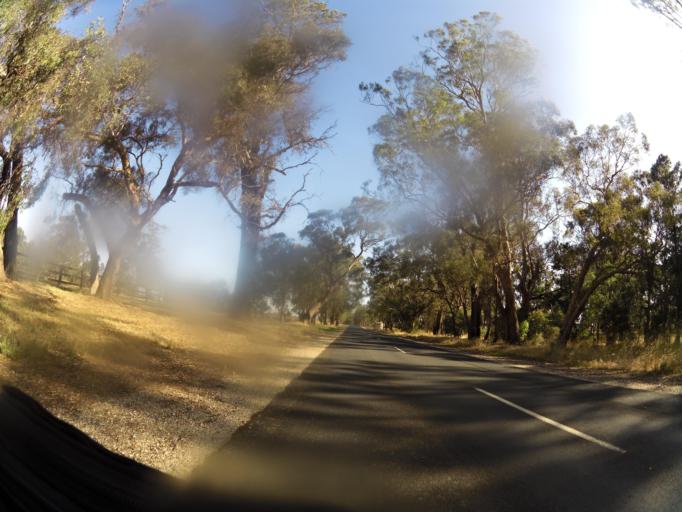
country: AU
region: Victoria
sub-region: Murrindindi
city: Kinglake West
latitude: -36.9609
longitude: 145.1078
